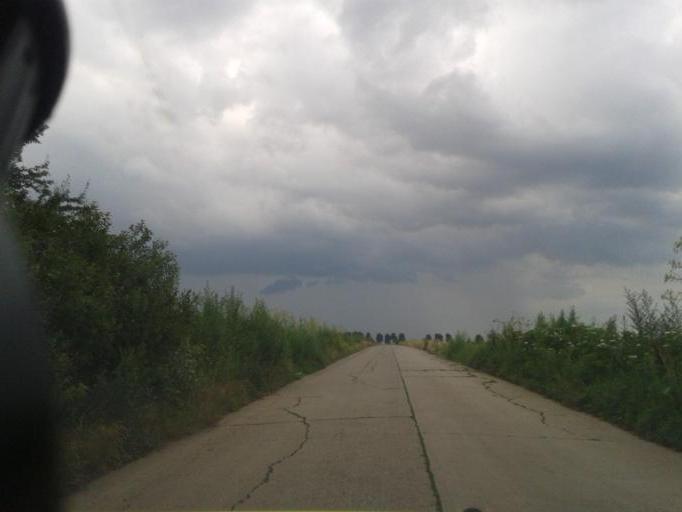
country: RO
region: Calarasi
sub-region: Comuna Fundulea
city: Fundulea
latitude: 44.5205
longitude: 26.4868
